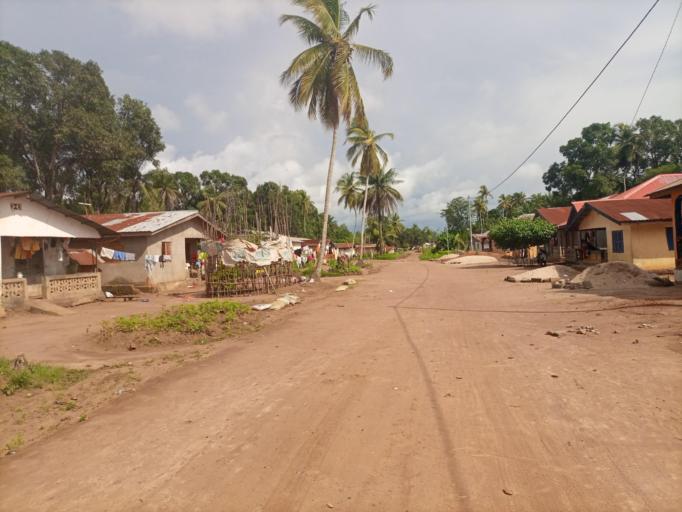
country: SL
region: Northern Province
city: Masoyila
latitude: 8.6160
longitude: -13.1715
